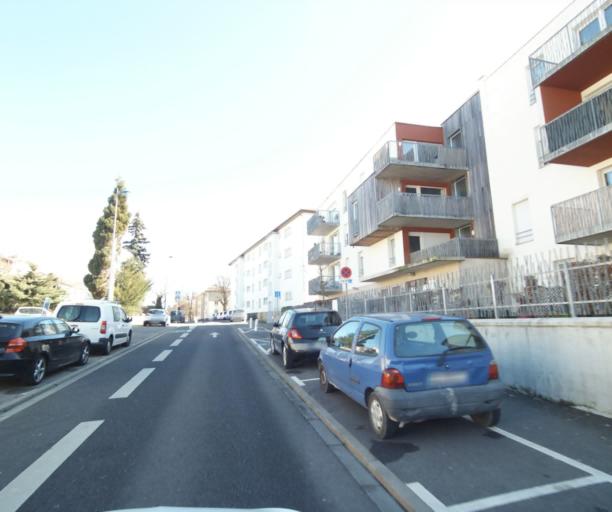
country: FR
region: Lorraine
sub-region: Departement de Meurthe-et-Moselle
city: Saint-Max
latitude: 48.7036
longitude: 6.1974
